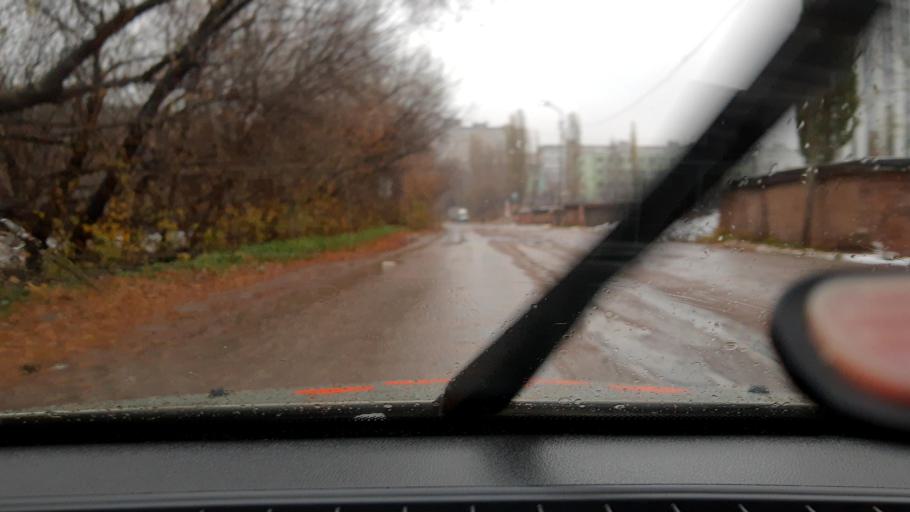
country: RU
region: Bashkortostan
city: Ufa
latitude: 54.7260
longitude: 55.9991
